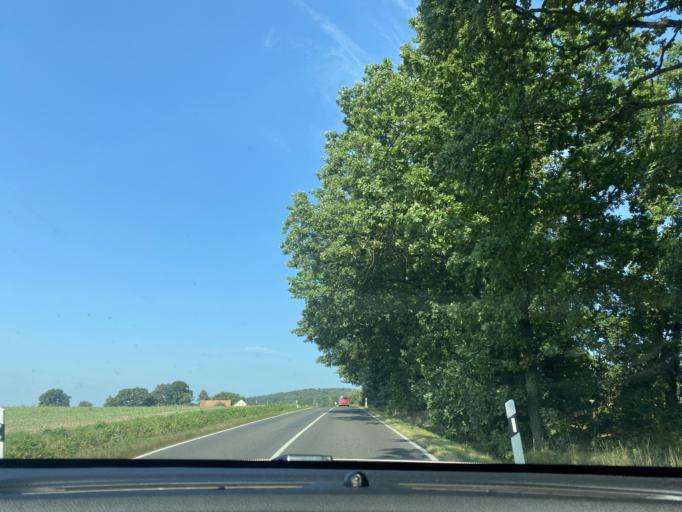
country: DE
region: Saxony
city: Reichenbach
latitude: 51.1565
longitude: 14.7959
